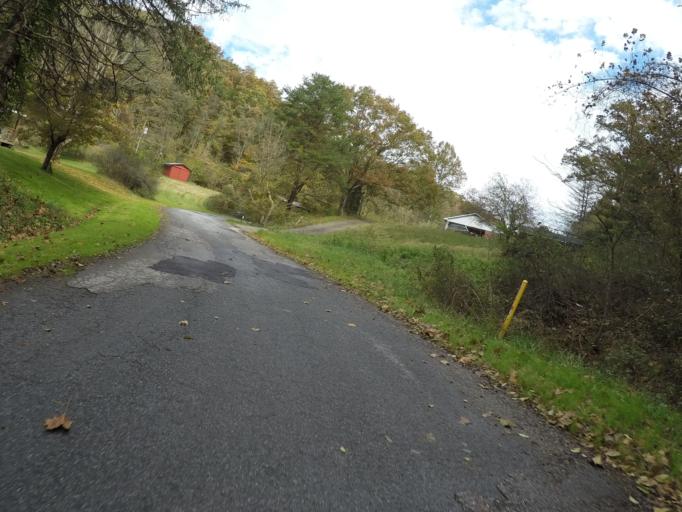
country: US
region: West Virginia
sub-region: Wayne County
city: Lavalette
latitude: 38.3449
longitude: -82.4491
